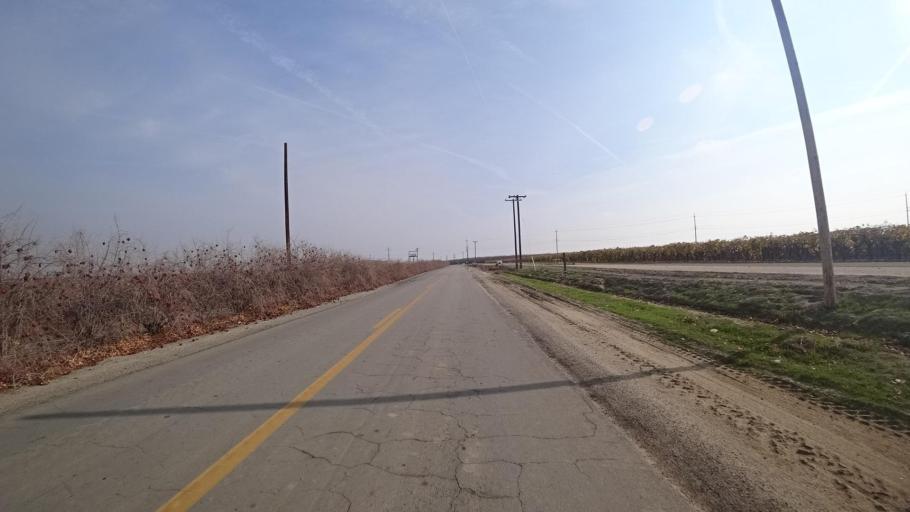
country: US
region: California
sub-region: Kern County
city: Lebec
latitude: 35.0314
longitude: -118.9392
